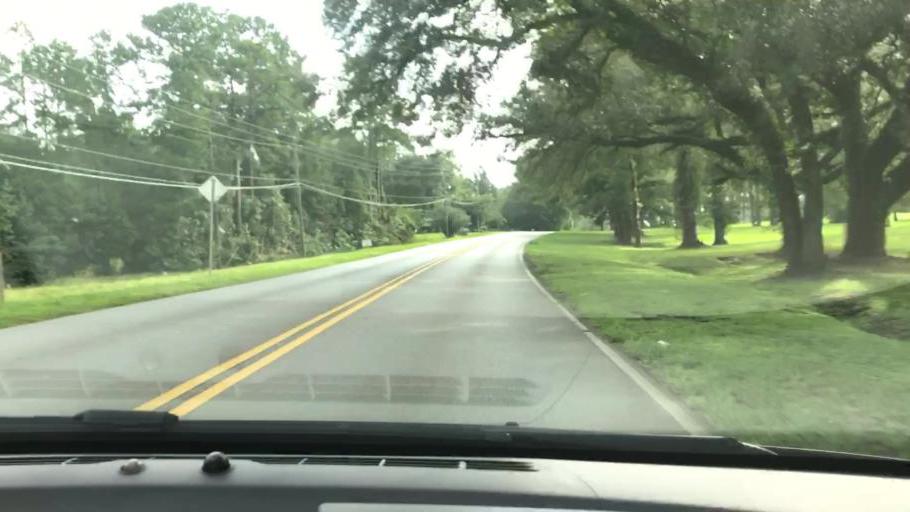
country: US
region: Florida
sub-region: Jackson County
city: Marianna
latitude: 30.7692
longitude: -85.2458
